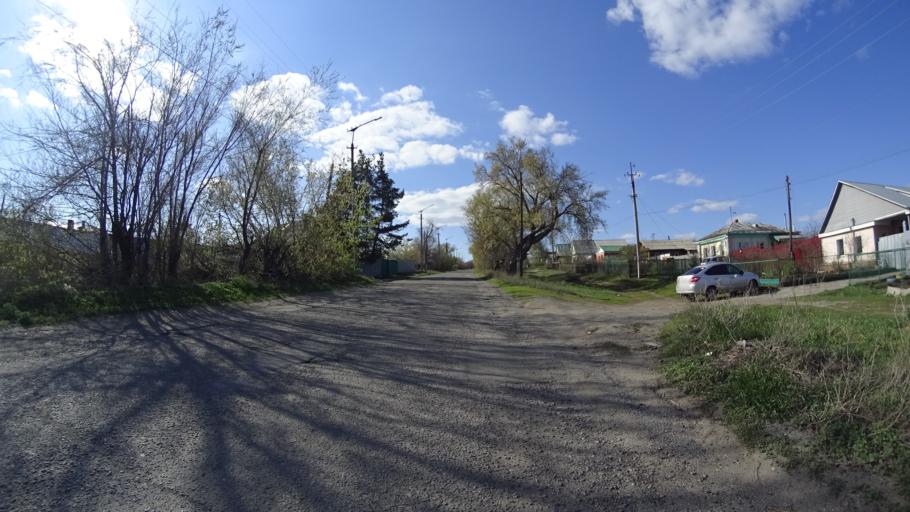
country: RU
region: Chelyabinsk
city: Troitsk
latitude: 54.0978
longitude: 61.5607
